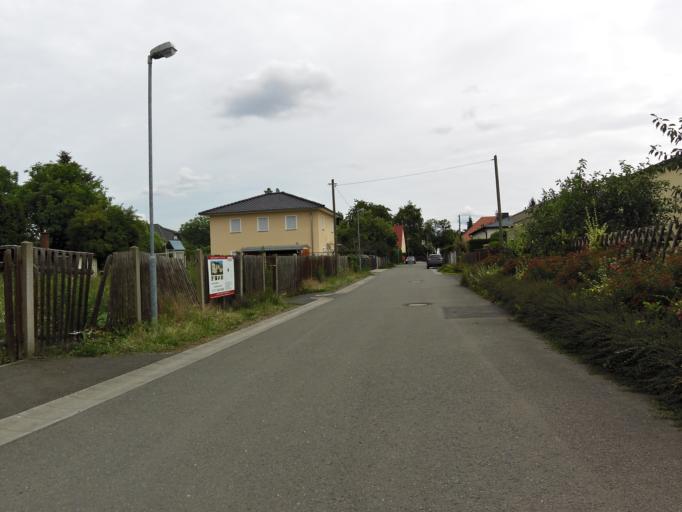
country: DE
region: Saxony
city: Rackwitz
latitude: 51.4009
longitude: 12.3819
